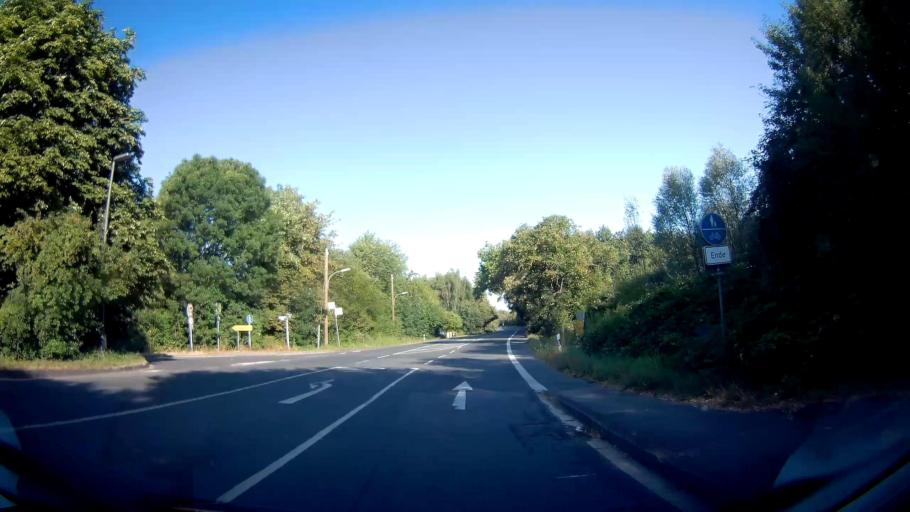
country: DE
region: North Rhine-Westphalia
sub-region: Regierungsbezirk Arnsberg
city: Dortmund
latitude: 51.5552
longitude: 7.4258
